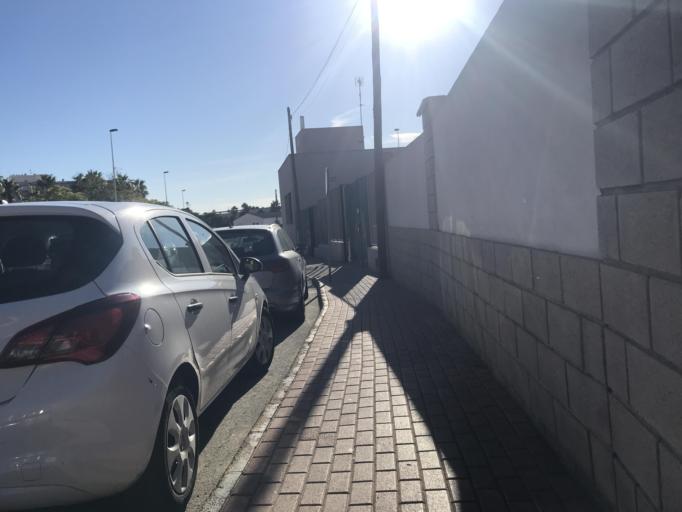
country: ES
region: Valencia
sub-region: Provincia de Alicante
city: Torrevieja
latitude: 37.9793
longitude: -0.6911
